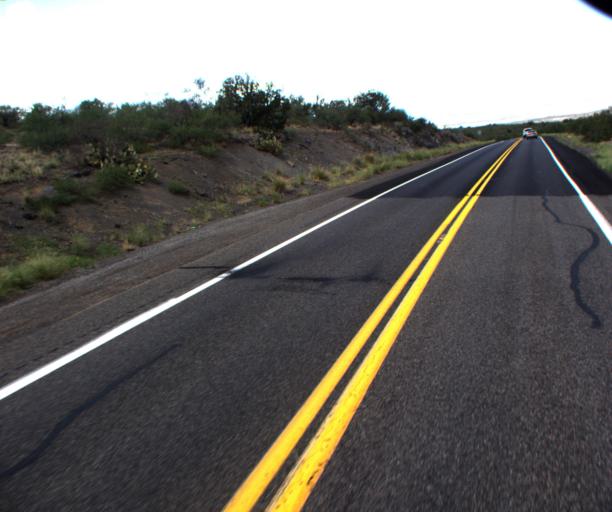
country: US
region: Arizona
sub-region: Yavapai County
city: Lake Montezuma
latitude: 34.5051
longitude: -111.7280
